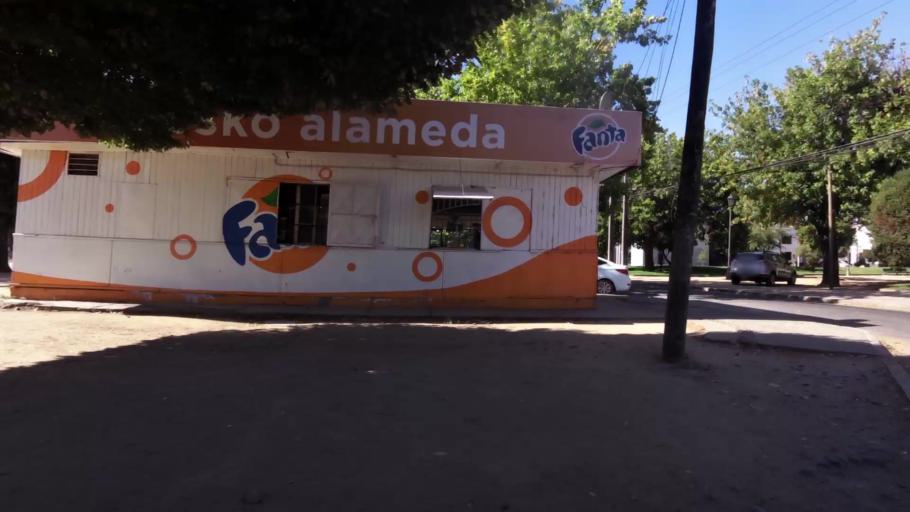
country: CL
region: Maule
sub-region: Provincia de Talca
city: Talca
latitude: -35.4220
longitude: -71.6678
